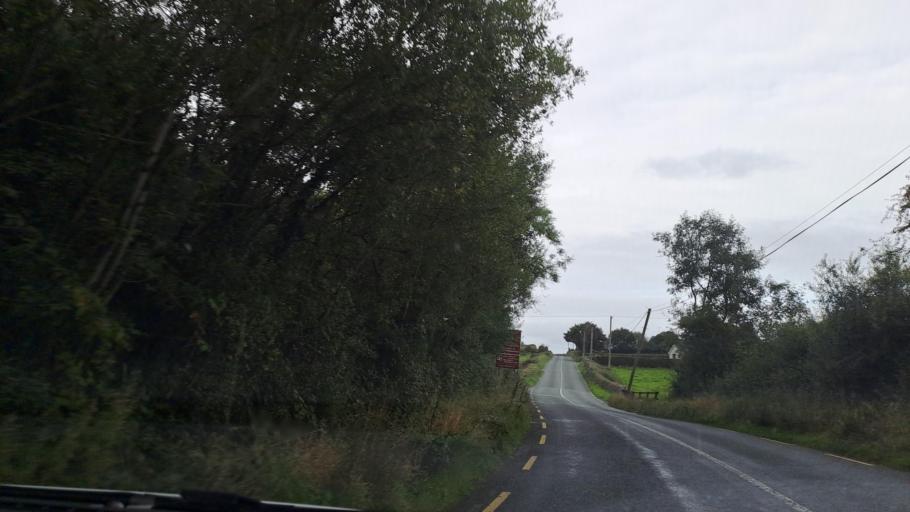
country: IE
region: Ulster
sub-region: An Cabhan
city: Bailieborough
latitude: 54.0145
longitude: -6.9099
